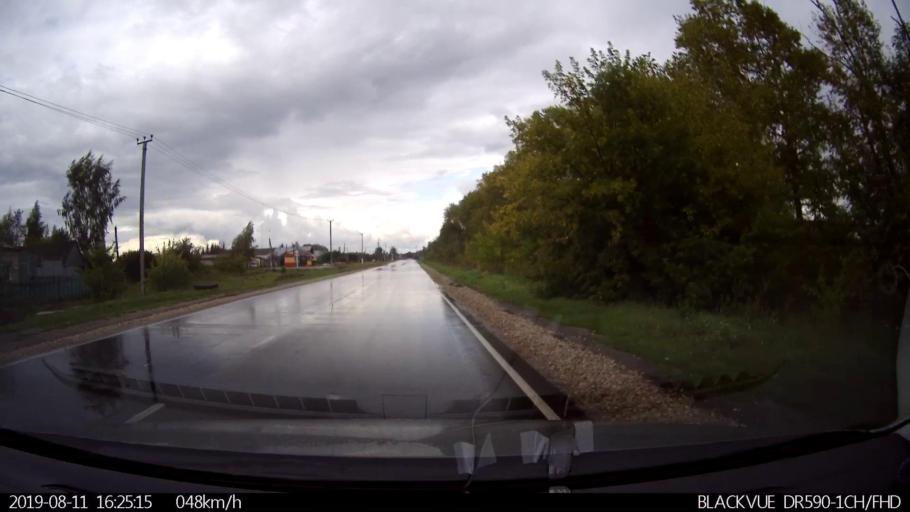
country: RU
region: Ulyanovsk
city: Mayna
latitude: 54.1048
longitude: 47.6022
